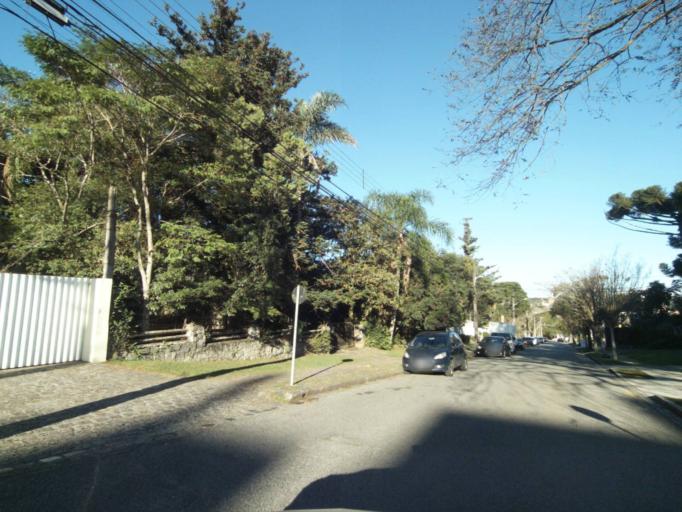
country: BR
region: Parana
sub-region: Curitiba
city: Curitiba
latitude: -25.4157
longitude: -49.2510
